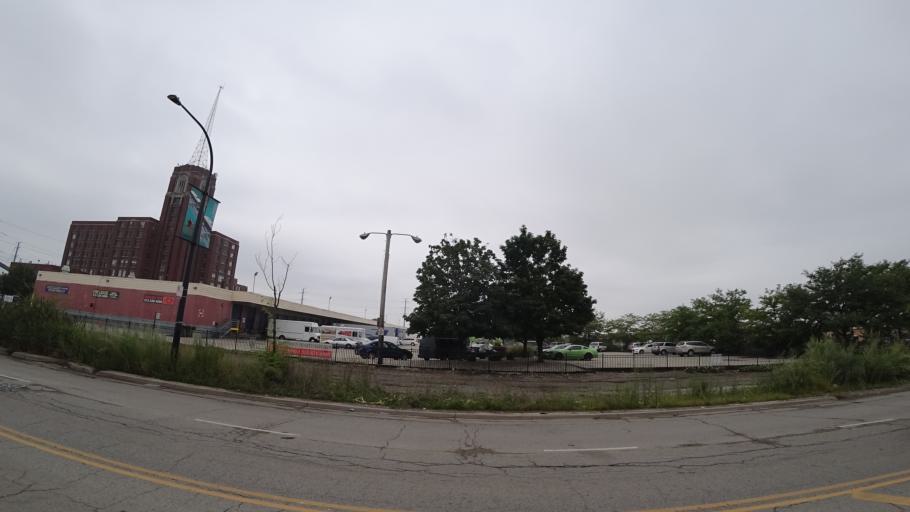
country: US
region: Illinois
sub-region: Cook County
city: Chicago
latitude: 41.8524
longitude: -87.6599
